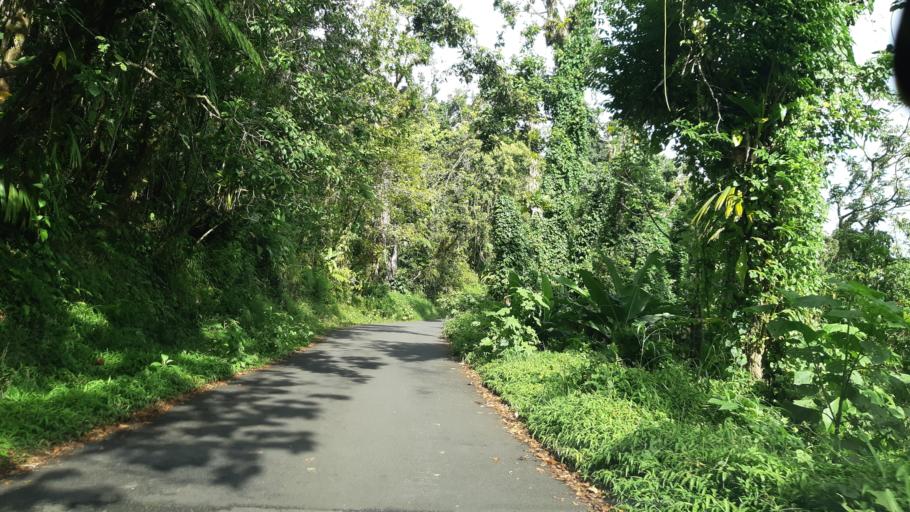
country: GP
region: Guadeloupe
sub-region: Guadeloupe
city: Saint-Claude
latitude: 16.0310
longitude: -61.6800
